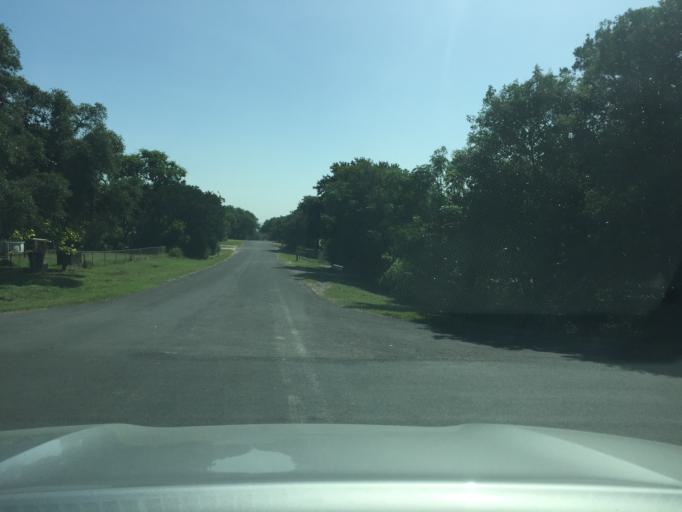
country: US
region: Texas
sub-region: Bexar County
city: Timberwood Park
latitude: 29.7086
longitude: -98.4773
